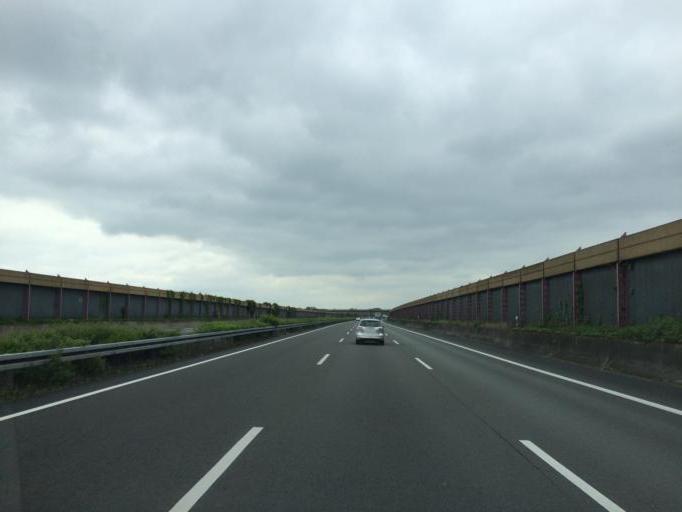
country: DE
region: Lower Saxony
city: Peine
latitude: 52.3365
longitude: 10.2536
